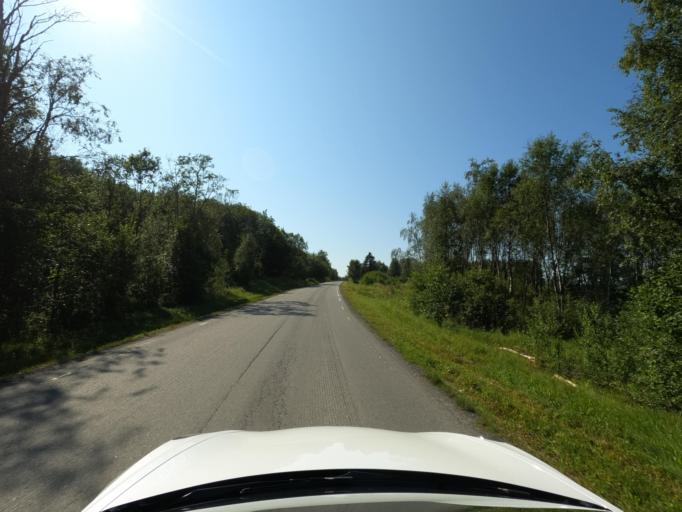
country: NO
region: Nordland
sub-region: Ballangen
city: Ballangen
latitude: 68.3609
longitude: 16.8782
